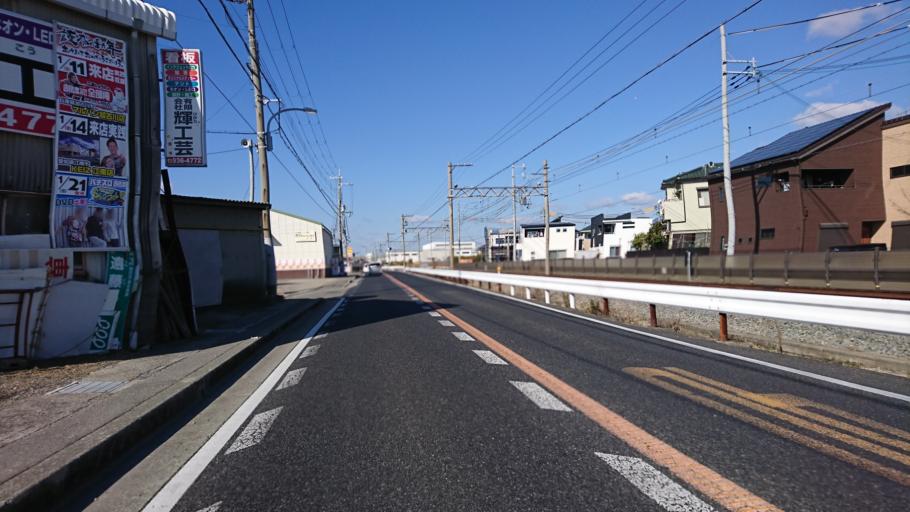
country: JP
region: Hyogo
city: Akashi
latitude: 34.6725
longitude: 134.9336
